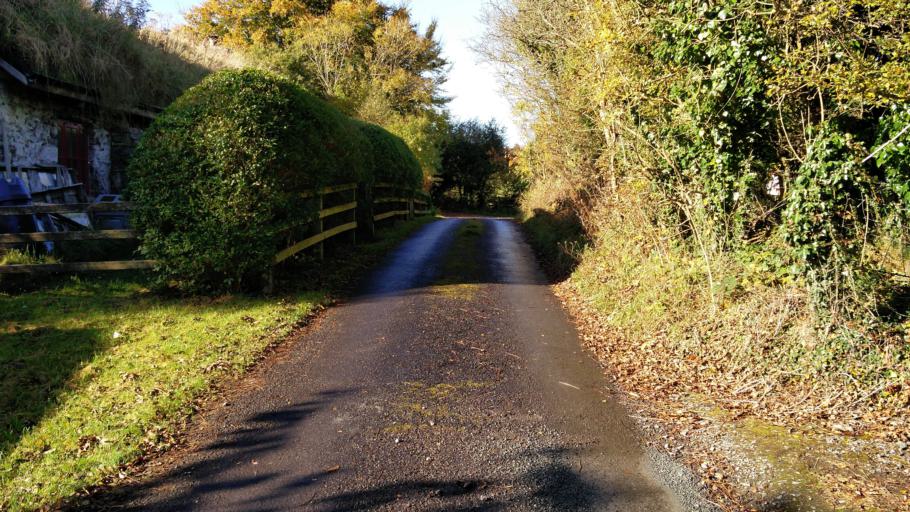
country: IE
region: Connaught
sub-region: Maigh Eo
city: Westport
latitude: 53.7803
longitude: -9.4460
